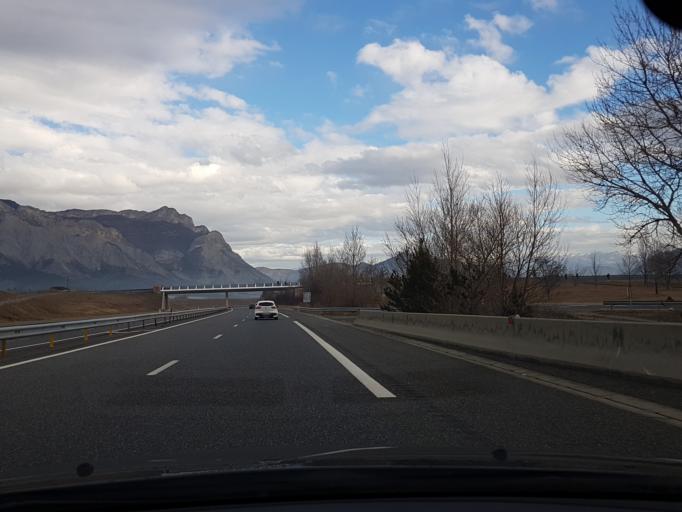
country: FR
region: Provence-Alpes-Cote d'Azur
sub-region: Departement des Hautes-Alpes
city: Laragne-Monteglin
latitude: 44.3653
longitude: 5.9224
